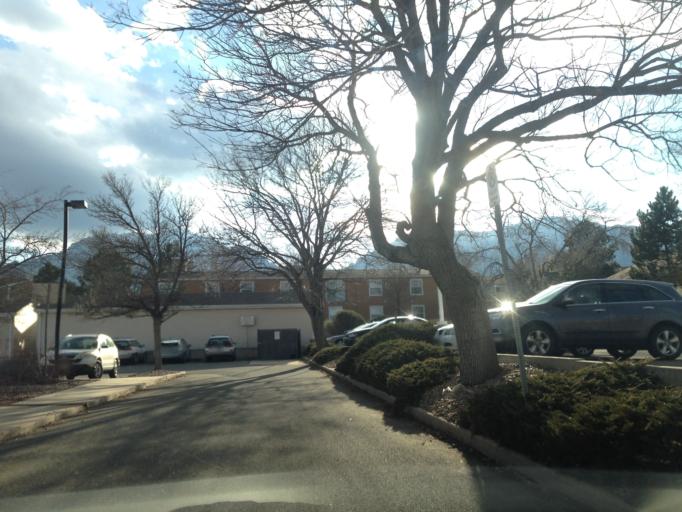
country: US
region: Colorado
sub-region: Boulder County
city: Boulder
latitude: 39.9847
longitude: -105.2527
